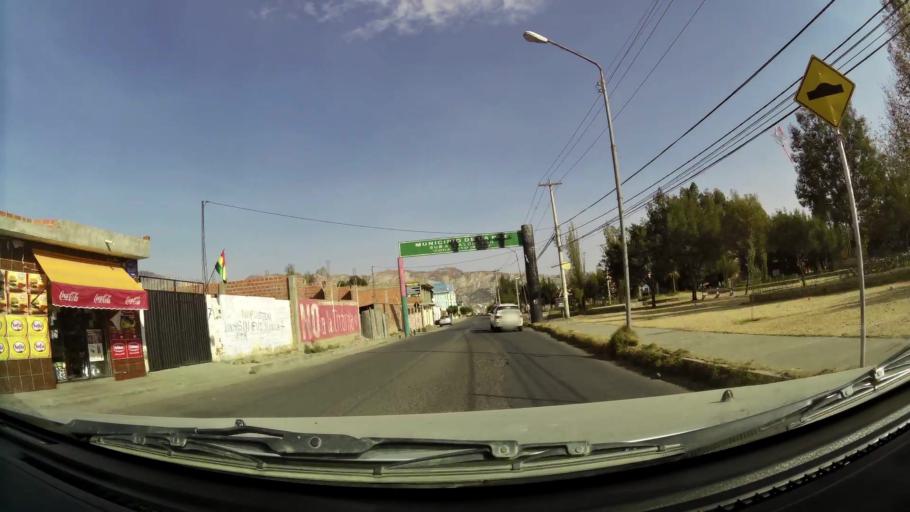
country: BO
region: La Paz
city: La Paz
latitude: -16.5254
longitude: -68.0799
